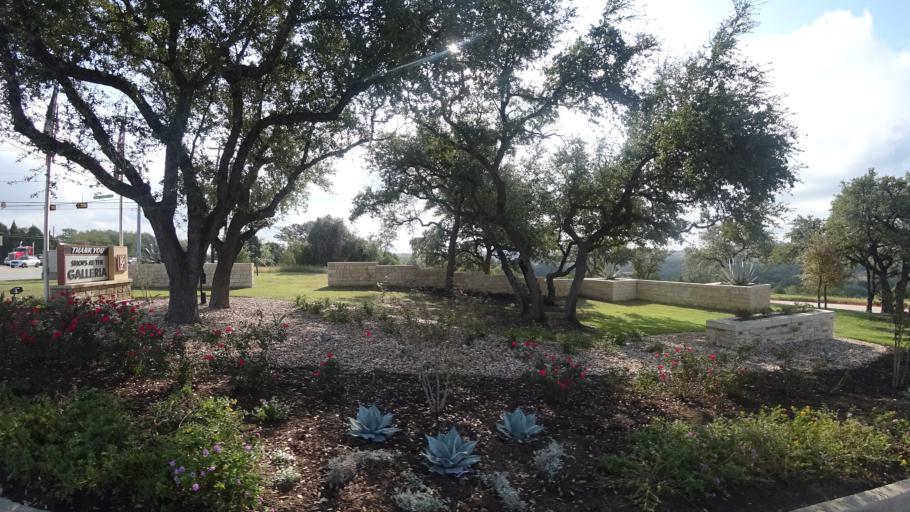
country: US
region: Texas
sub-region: Travis County
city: Bee Cave
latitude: 30.3048
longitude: -97.9363
